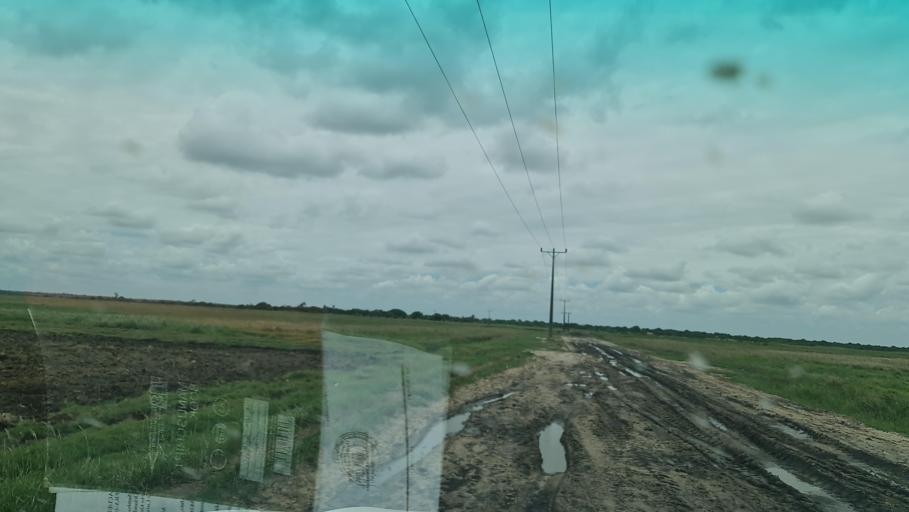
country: MZ
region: Maputo City
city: Maputo
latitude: -25.7101
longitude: 32.7031
